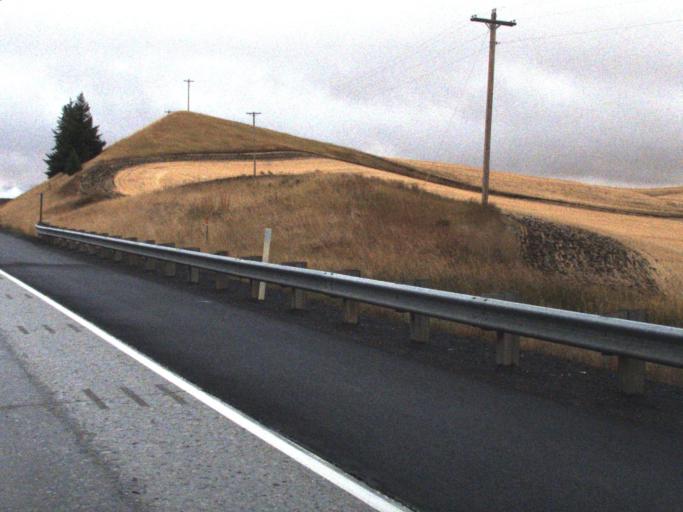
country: US
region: Washington
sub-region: Whitman County
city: Colfax
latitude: 47.0340
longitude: -117.3657
